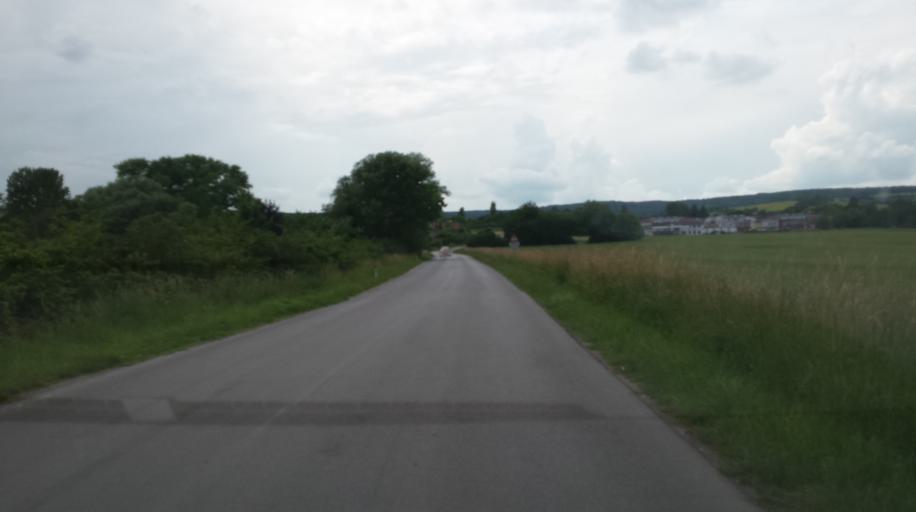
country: AT
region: Lower Austria
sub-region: Politischer Bezirk Mistelbach
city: Wolkersdorf im Weinviertel
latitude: 48.4188
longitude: 16.4999
